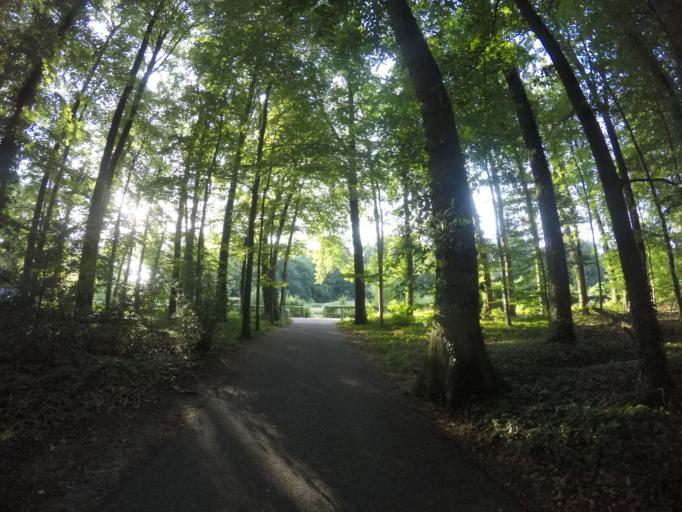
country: NL
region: Gelderland
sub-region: Gemeente Arnhem
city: Burgemeesterswijk
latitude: 51.9948
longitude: 5.9005
